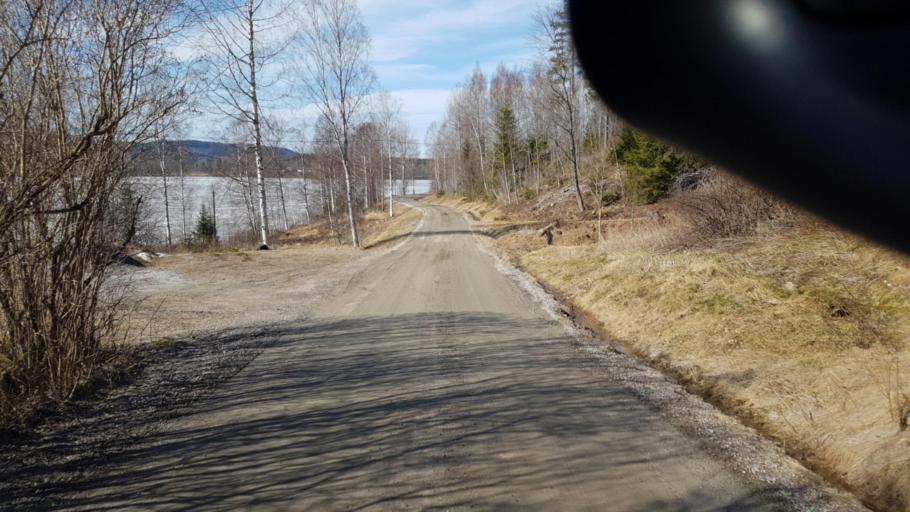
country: SE
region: Vaermland
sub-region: Arvika Kommun
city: Arvika
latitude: 59.7341
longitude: 12.8322
